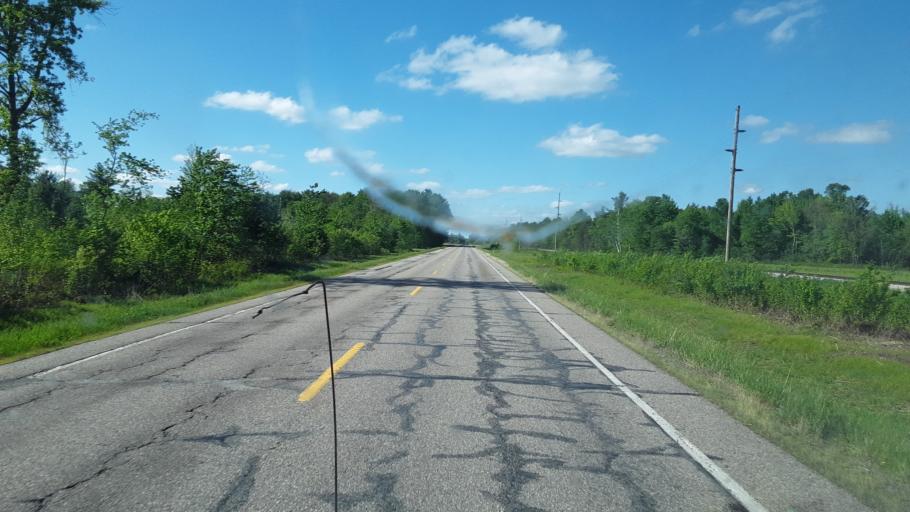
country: US
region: Wisconsin
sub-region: Wood County
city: Nekoosa
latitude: 44.2349
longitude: -90.1387
